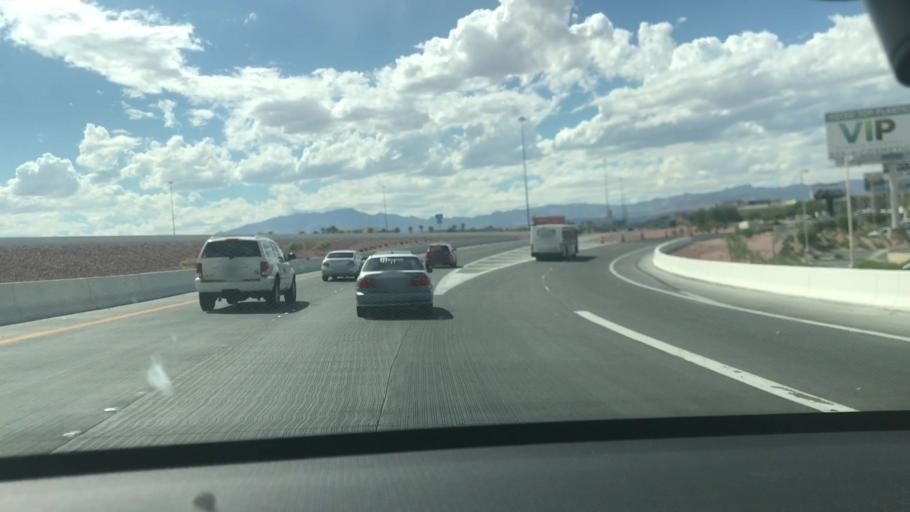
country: US
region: Nevada
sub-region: Clark County
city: Paradise
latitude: 36.0637
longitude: -115.1510
